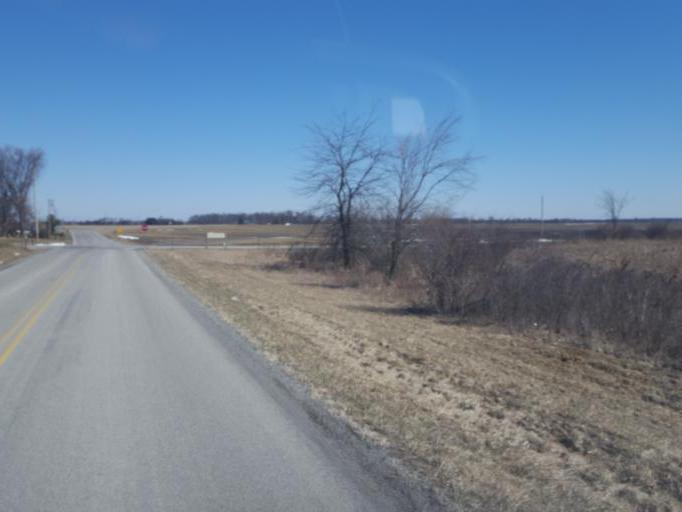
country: US
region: Ohio
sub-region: Wyandot County
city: Upper Sandusky
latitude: 40.7373
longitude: -83.2934
